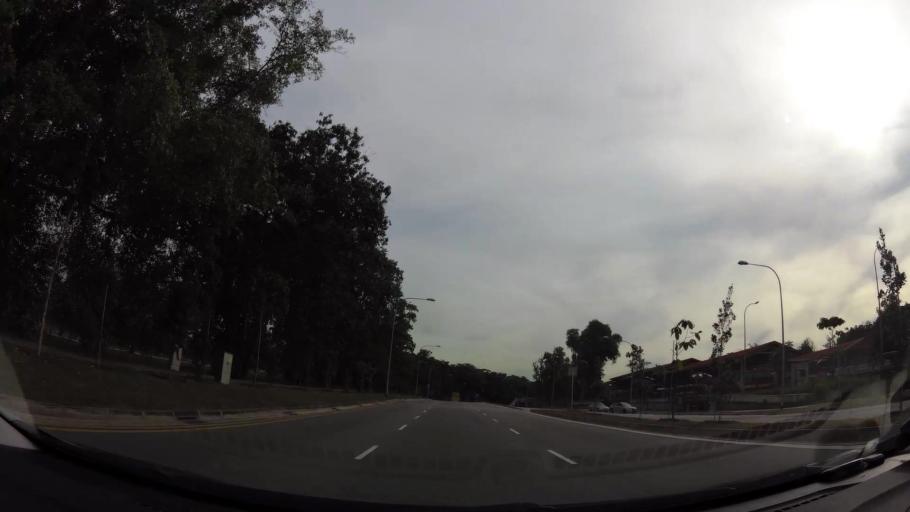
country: MY
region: Johor
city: Johor Bahru
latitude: 1.3689
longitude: 103.6941
